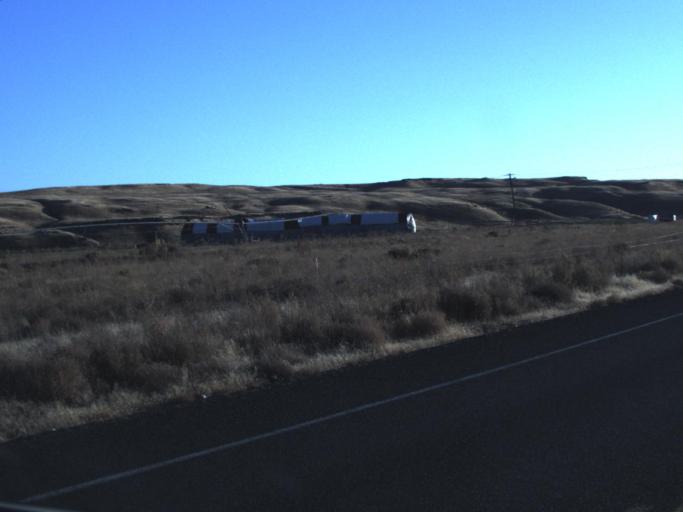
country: US
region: Washington
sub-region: Franklin County
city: Connell
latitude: 46.6845
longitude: -118.4412
